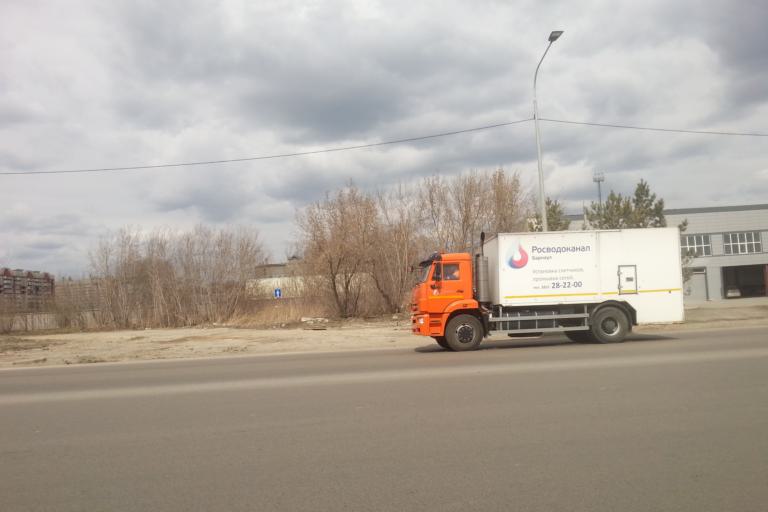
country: RU
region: Altai Krai
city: Novosilikatnyy
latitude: 53.3271
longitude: 83.6940
